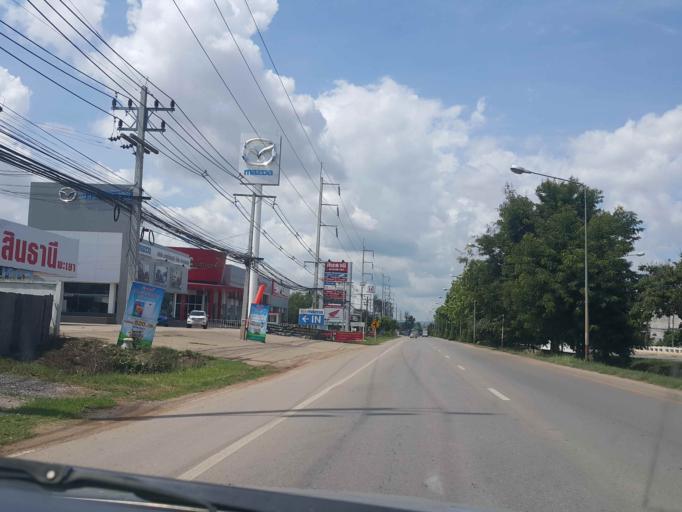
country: TH
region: Phayao
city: Phayao
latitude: 19.1515
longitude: 99.9128
